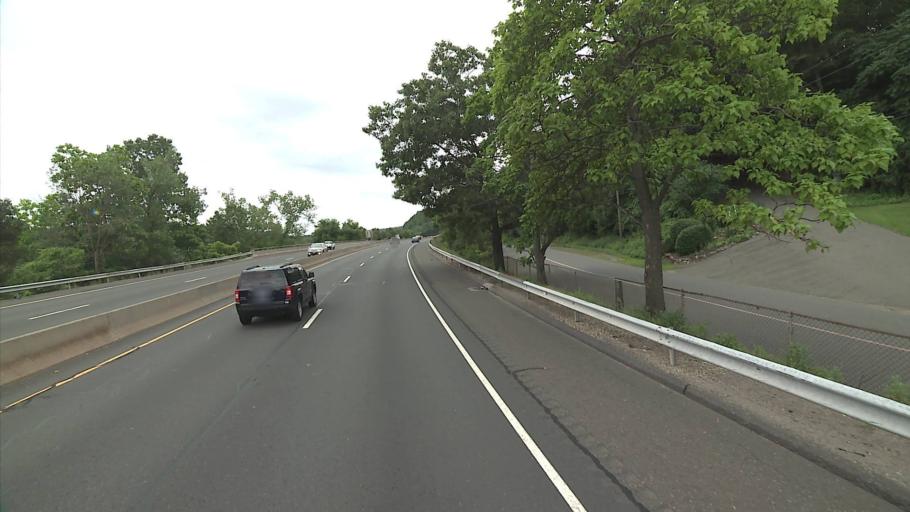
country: US
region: Connecticut
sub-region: New Haven County
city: Seymour
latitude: 41.3828
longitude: -73.0787
